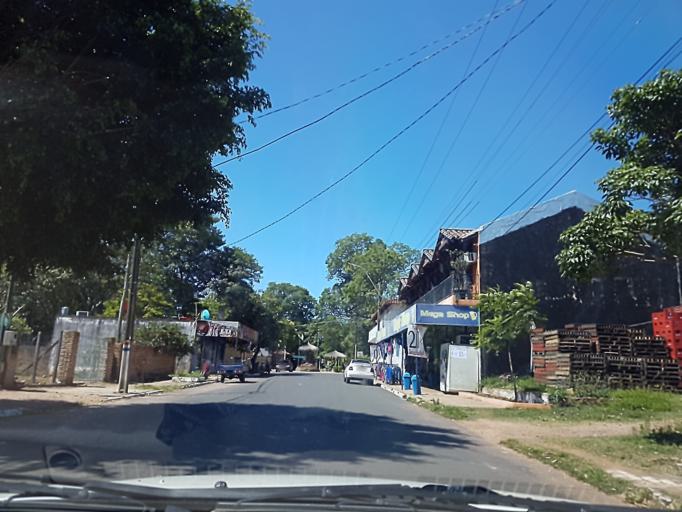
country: PY
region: Cordillera
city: Atyra
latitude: -25.2796
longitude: -57.1740
